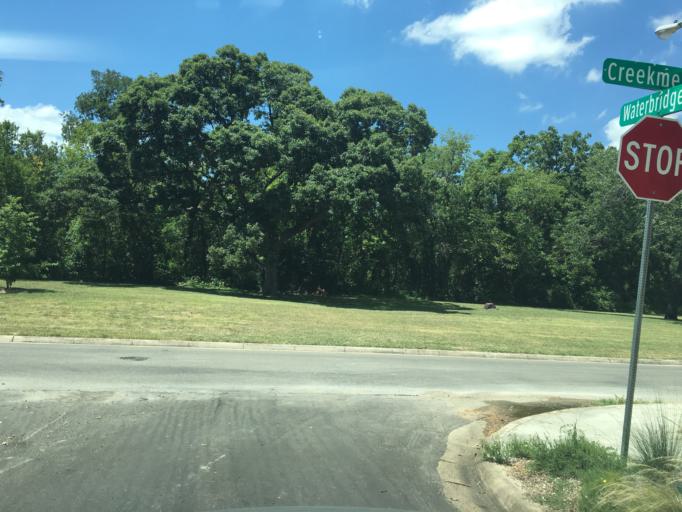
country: US
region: Texas
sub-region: Dallas County
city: Garland
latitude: 32.8509
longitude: -96.6918
